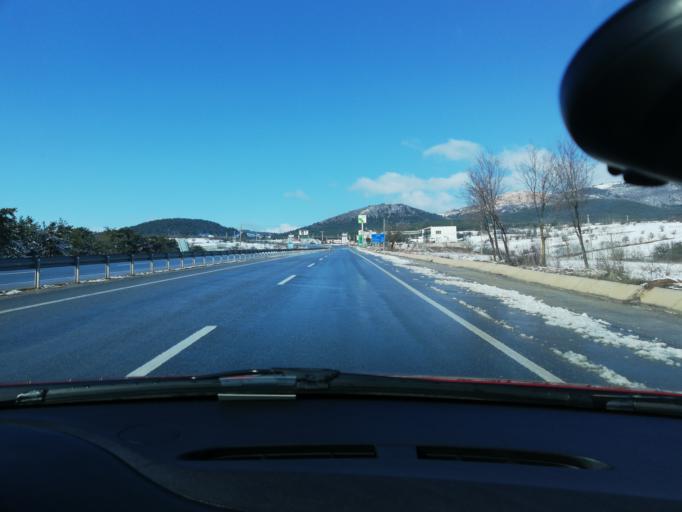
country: TR
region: Kastamonu
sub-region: Cide
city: Kastamonu
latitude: 41.3629
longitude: 33.7205
